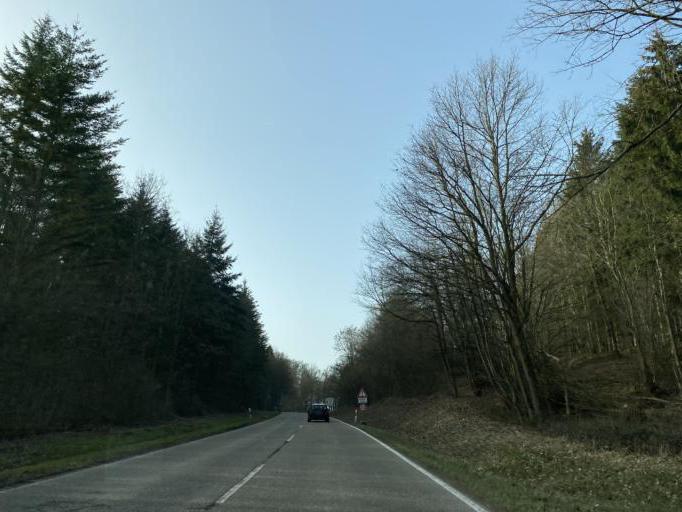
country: DE
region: Baden-Wuerttemberg
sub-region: Karlsruhe Region
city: Wiernsheim
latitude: 48.8769
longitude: 8.8355
